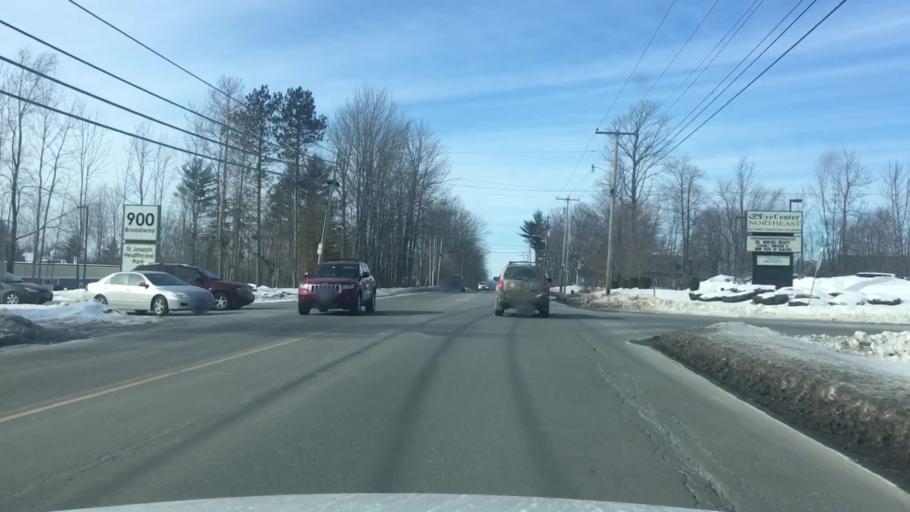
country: US
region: Maine
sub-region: Penobscot County
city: Bangor
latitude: 44.8310
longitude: -68.7864
